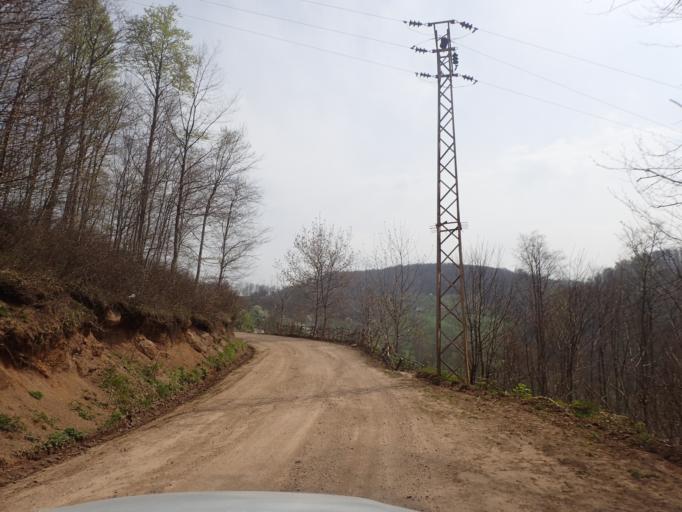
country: TR
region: Ordu
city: Aybasti
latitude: 40.7057
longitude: 37.2852
